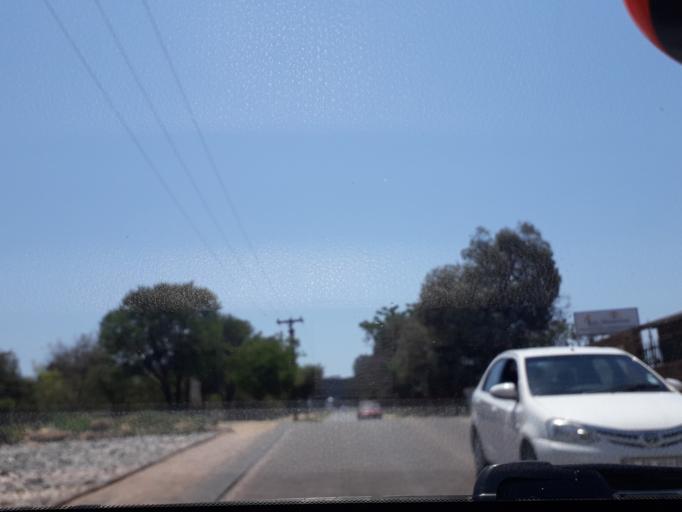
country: ZA
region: Gauteng
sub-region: City of Johannesburg Metropolitan Municipality
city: Midrand
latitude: -26.0203
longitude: 28.1319
